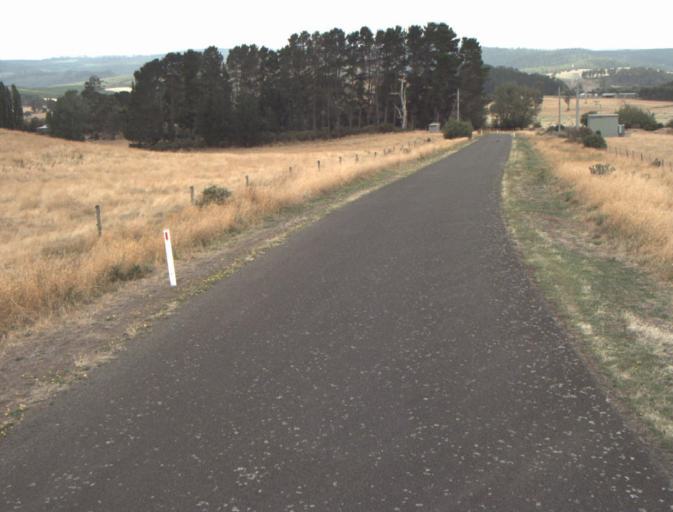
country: AU
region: Tasmania
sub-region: Northern Midlands
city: Evandale
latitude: -41.5072
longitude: 147.4811
